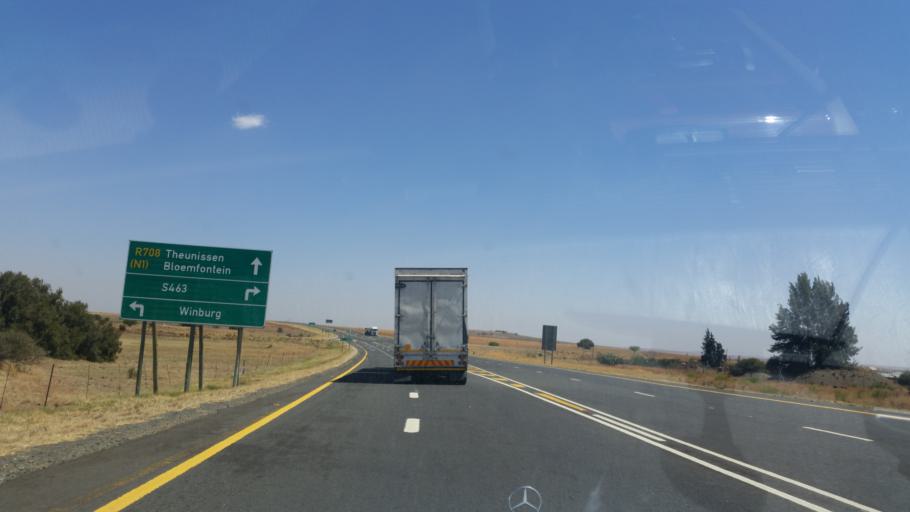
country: ZA
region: Orange Free State
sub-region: Lejweleputswa District Municipality
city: Winburg
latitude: -28.4944
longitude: 27.0374
